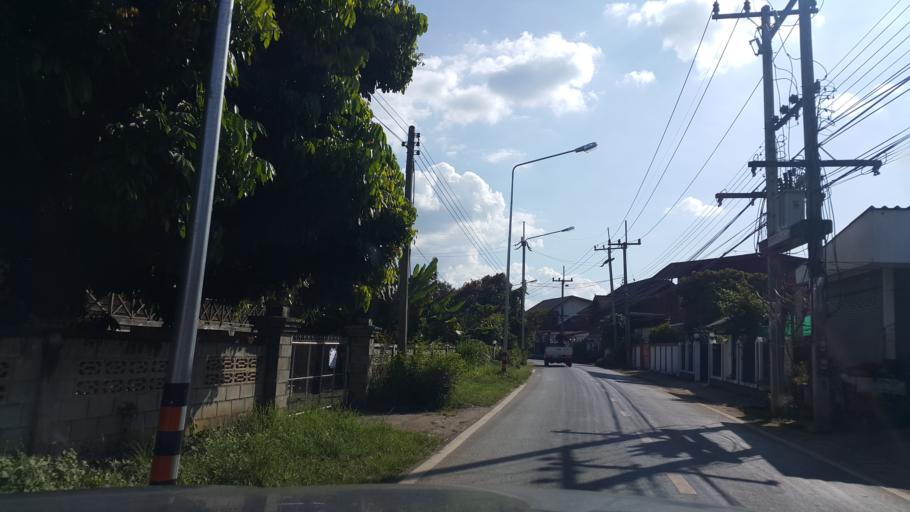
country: TH
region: Lamphun
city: Mae Tha
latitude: 18.5476
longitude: 99.2446
